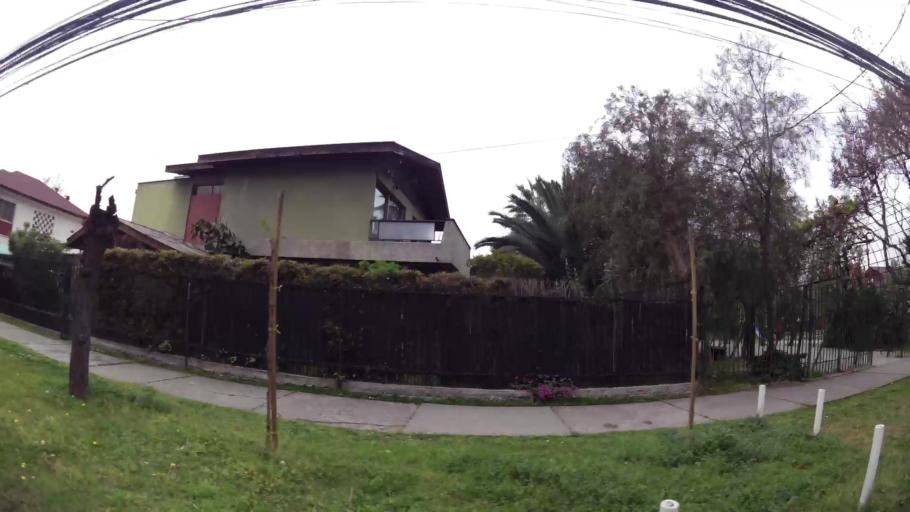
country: CL
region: Santiago Metropolitan
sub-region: Provincia de Santiago
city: Villa Presidente Frei, Nunoa, Santiago, Chile
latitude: -33.4595
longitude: -70.5884
